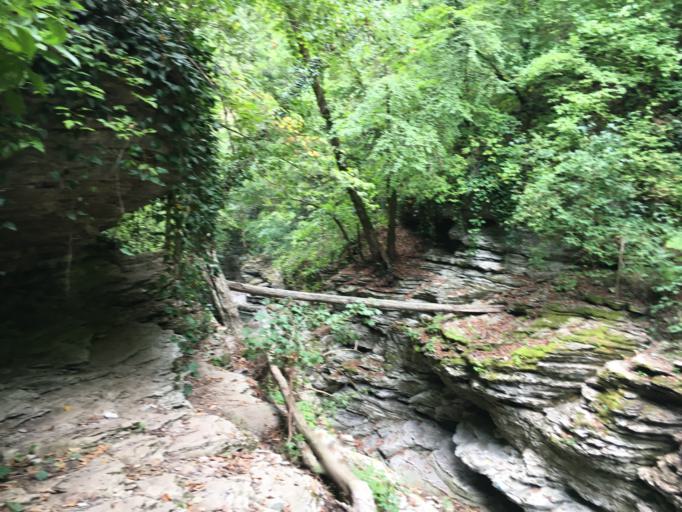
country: RU
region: Krasnodarskiy
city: Tuapse
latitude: 44.2627
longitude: 39.2066
